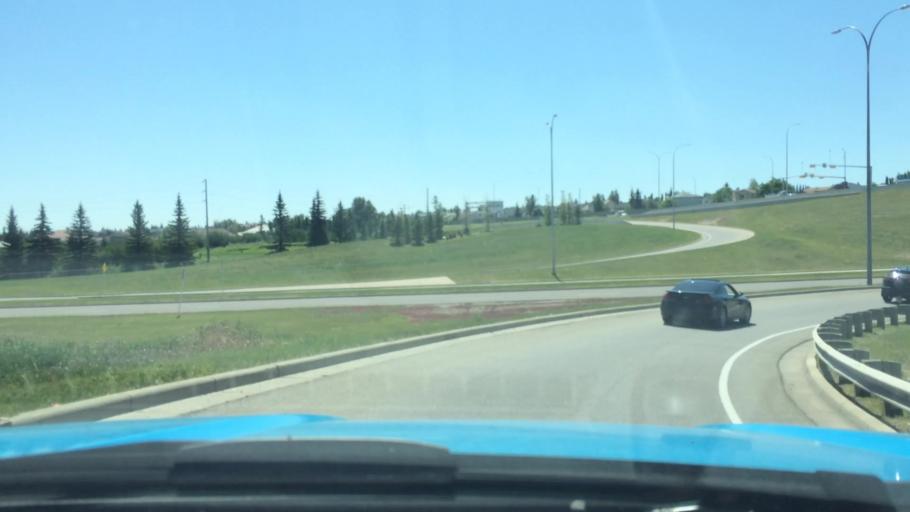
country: CA
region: Alberta
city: Calgary
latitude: 51.1448
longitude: -114.0914
